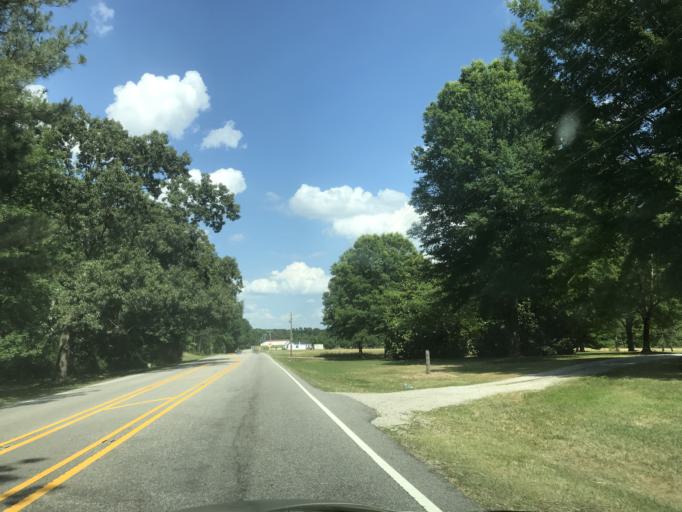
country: US
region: North Carolina
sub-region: Wake County
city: Rolesville
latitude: 35.9761
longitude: -78.3566
